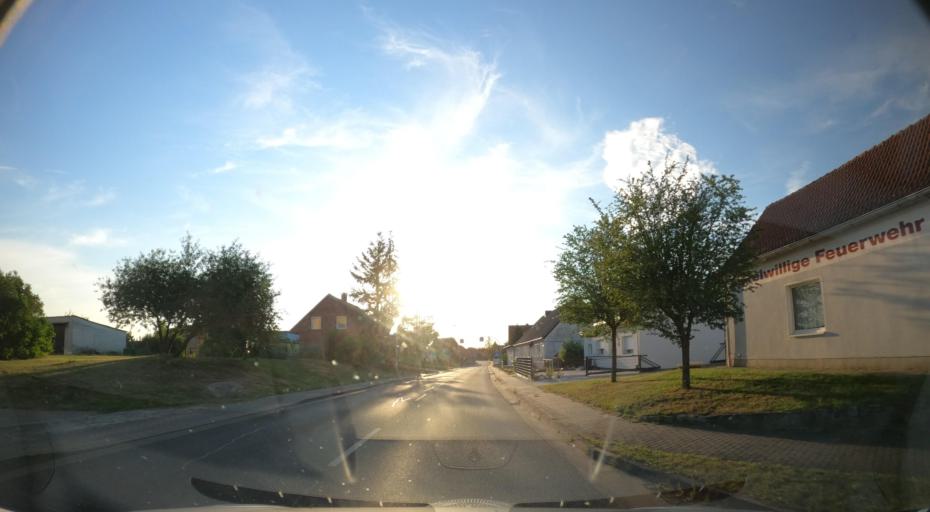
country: PL
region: West Pomeranian Voivodeship
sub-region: Powiat policki
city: Dobra
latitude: 53.4554
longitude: 14.3203
